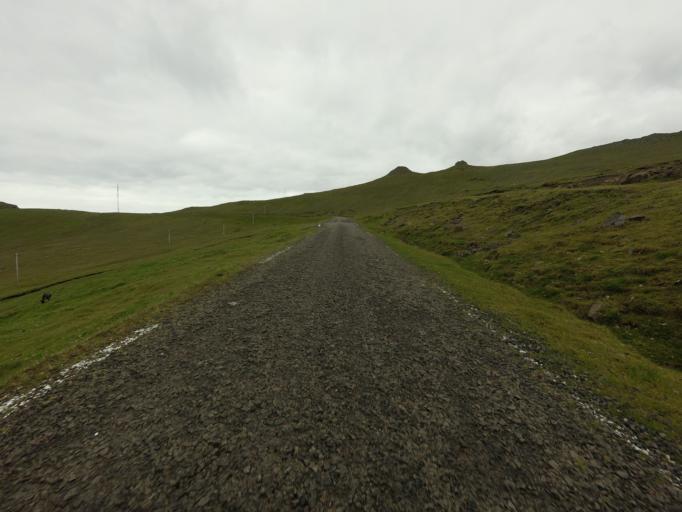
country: FO
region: Suduroy
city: Vagur
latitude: 61.4233
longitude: -6.7441
